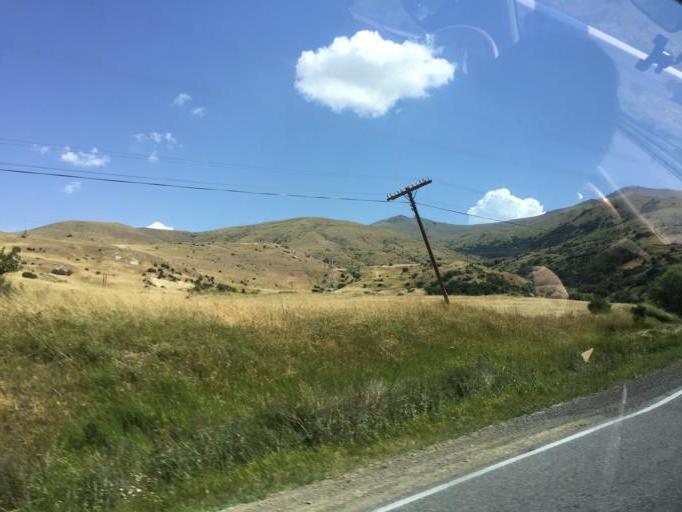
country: AM
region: Vayots' Dzori Marz
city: Jermuk
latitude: 39.7128
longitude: 45.6649
